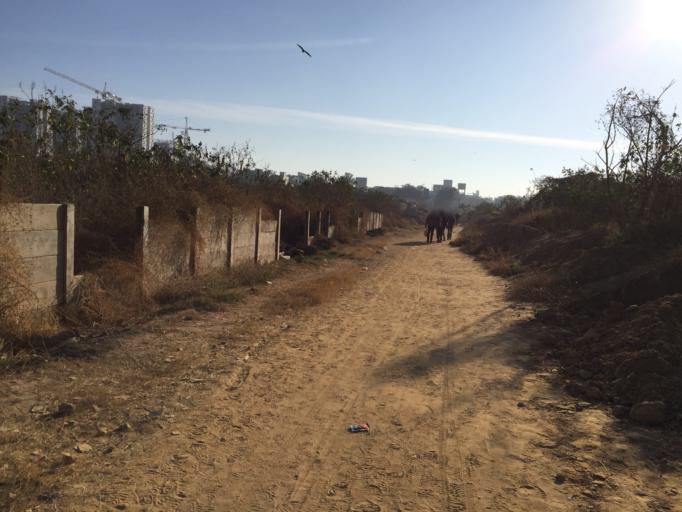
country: IN
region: Karnataka
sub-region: Bangalore Urban
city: Yelahanka
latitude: 13.0542
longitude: 77.6176
